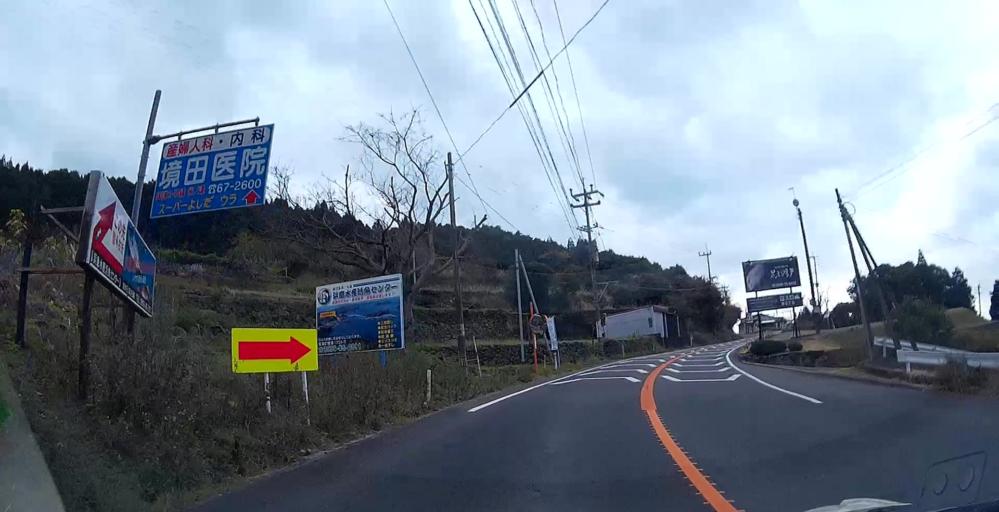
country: JP
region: Kagoshima
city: Akune
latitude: 32.1008
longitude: 130.1770
